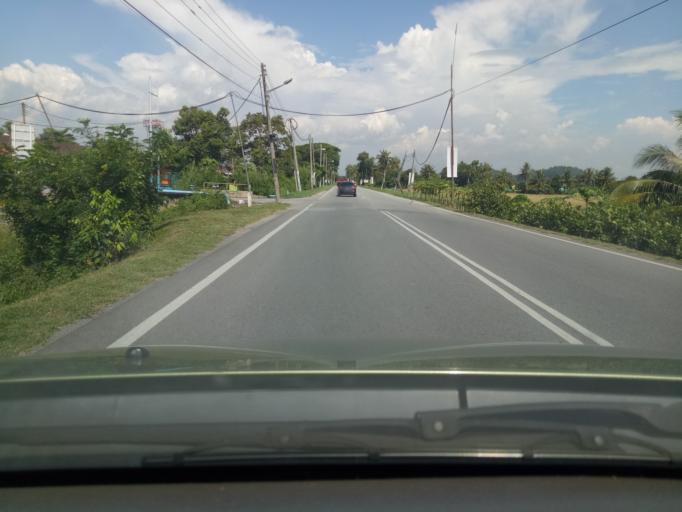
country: MY
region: Kedah
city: Alor Setar
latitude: 5.9740
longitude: 100.4056
